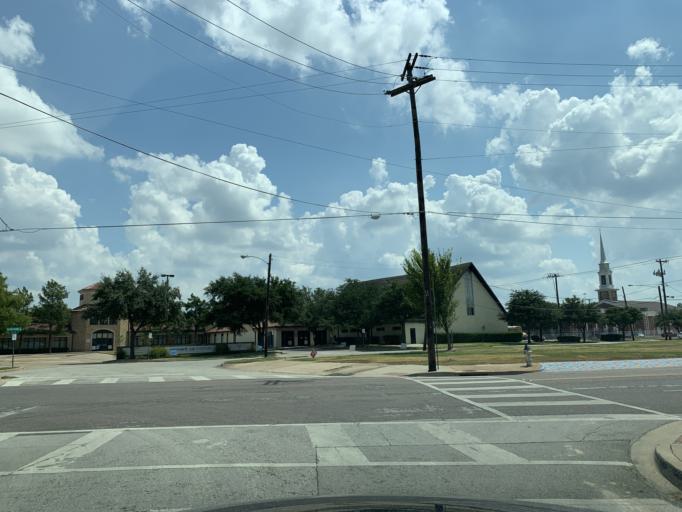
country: US
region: Texas
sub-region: Dallas County
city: Dallas
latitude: 32.7451
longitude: -96.8230
